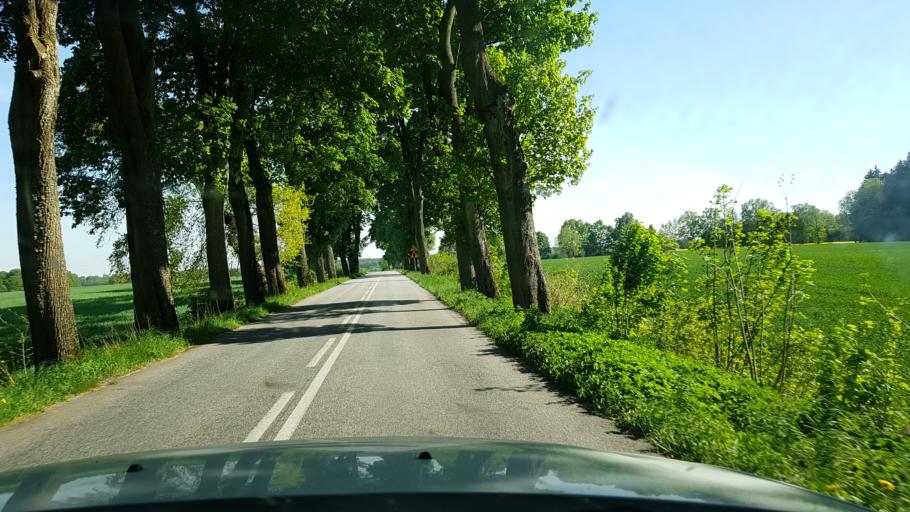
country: PL
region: West Pomeranian Voivodeship
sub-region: Powiat lobeski
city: Resko
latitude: 53.8322
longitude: 15.3875
